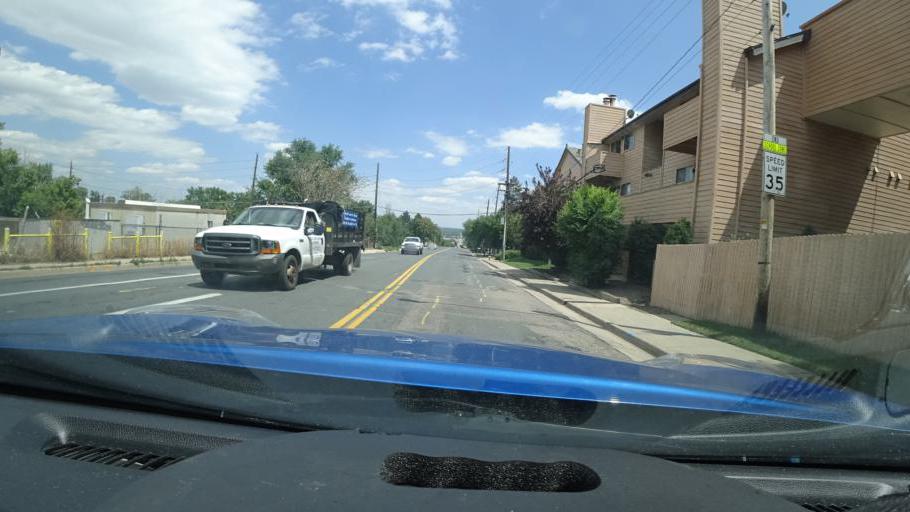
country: US
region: Colorado
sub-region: Arapahoe County
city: Sheridan
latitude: 39.6605
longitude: -105.0248
